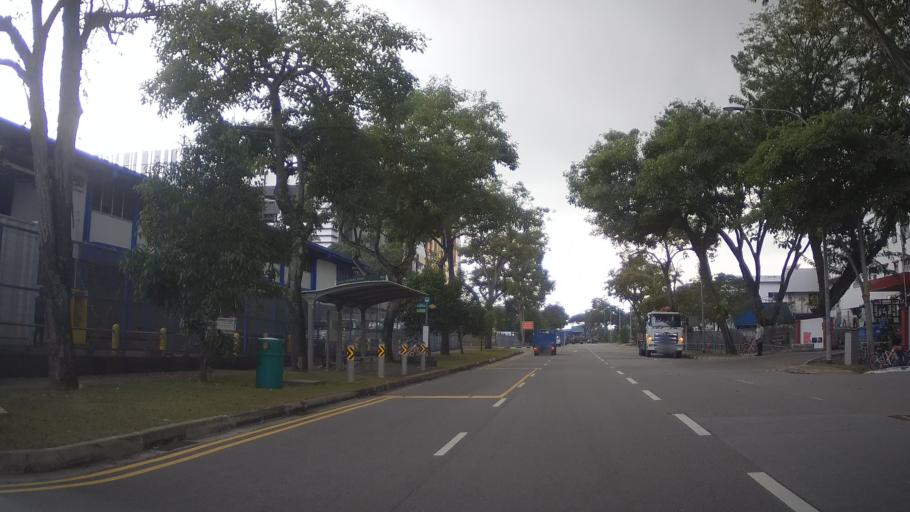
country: MY
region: Johor
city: Johor Bahru
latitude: 1.3257
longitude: 103.6838
